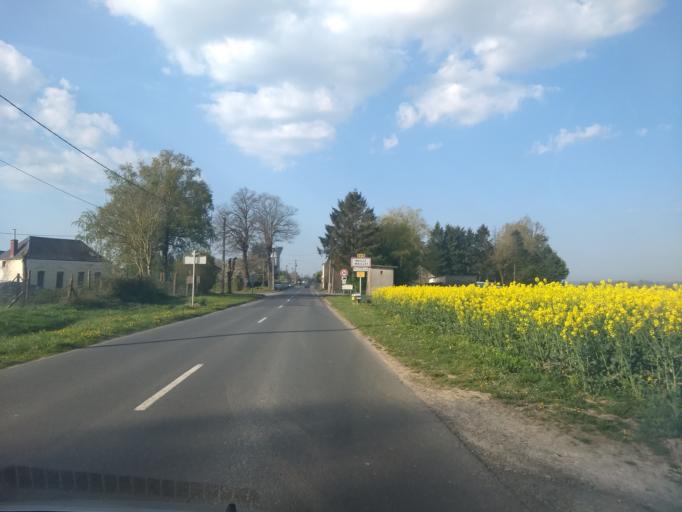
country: FR
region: Picardie
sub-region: Departement de la Somme
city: Albert
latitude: 50.0850
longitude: 2.6106
